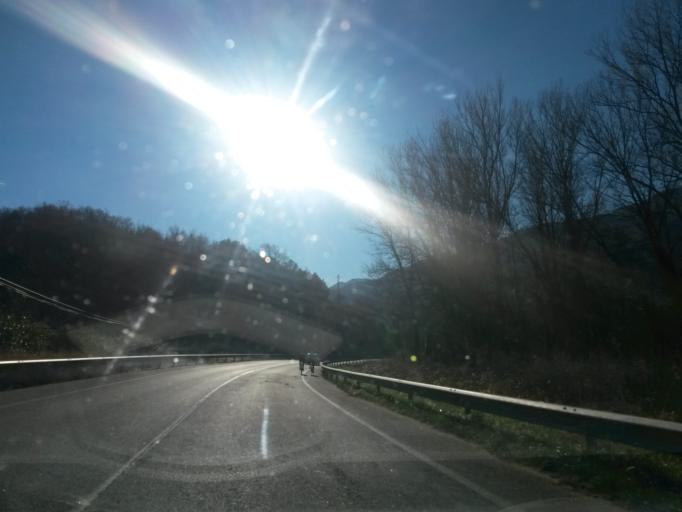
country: ES
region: Catalonia
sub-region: Provincia de Girona
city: Sant Feliu de Pallerols
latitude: 42.0865
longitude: 2.4973
